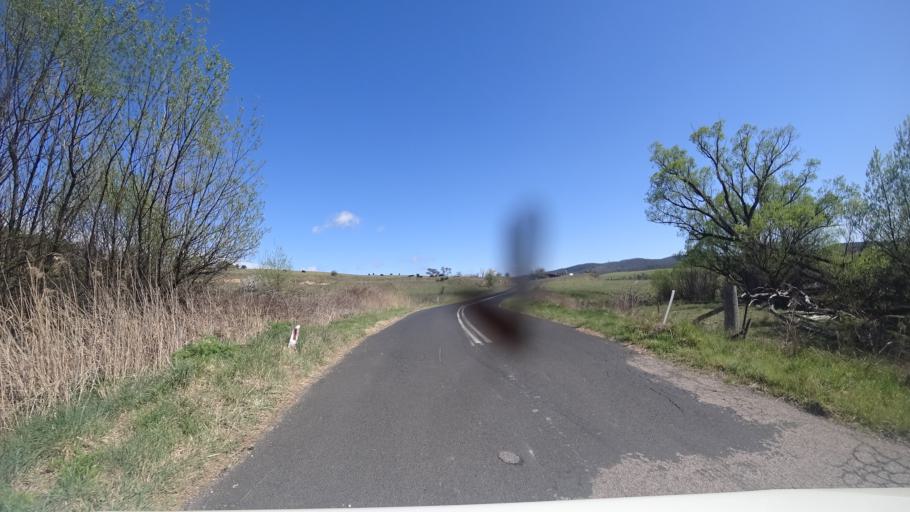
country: AU
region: New South Wales
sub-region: Lithgow
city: Bowenfels
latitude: -33.5180
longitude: 150.0080
